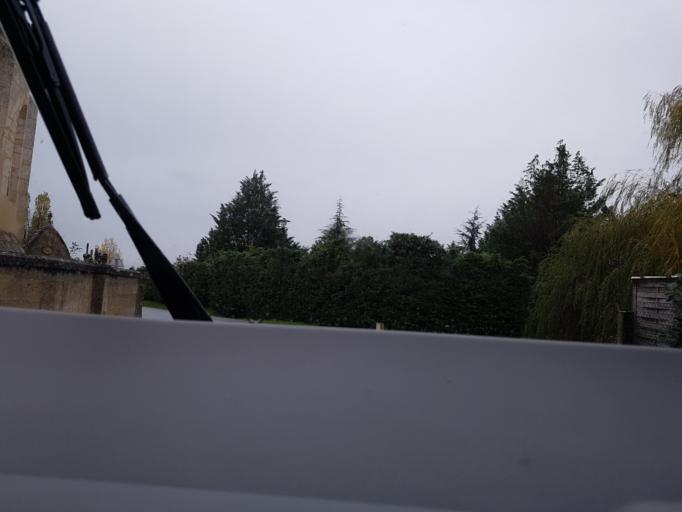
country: FR
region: Aquitaine
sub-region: Departement de la Gironde
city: Cezac
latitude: 45.1121
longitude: -0.4431
